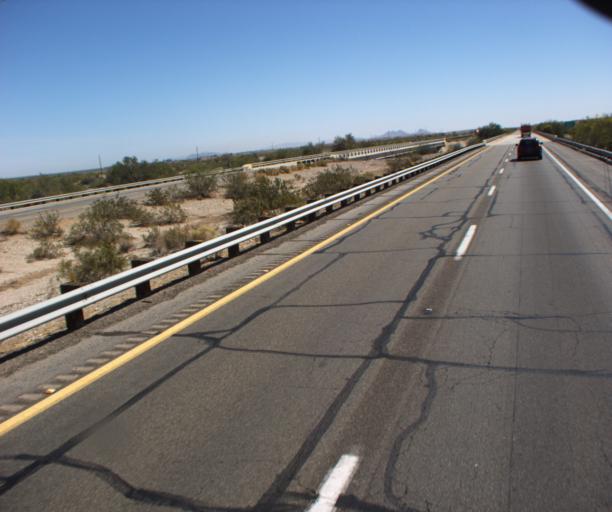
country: US
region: Arizona
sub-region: Yuma County
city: Wellton
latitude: 32.6598
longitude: -114.2547
